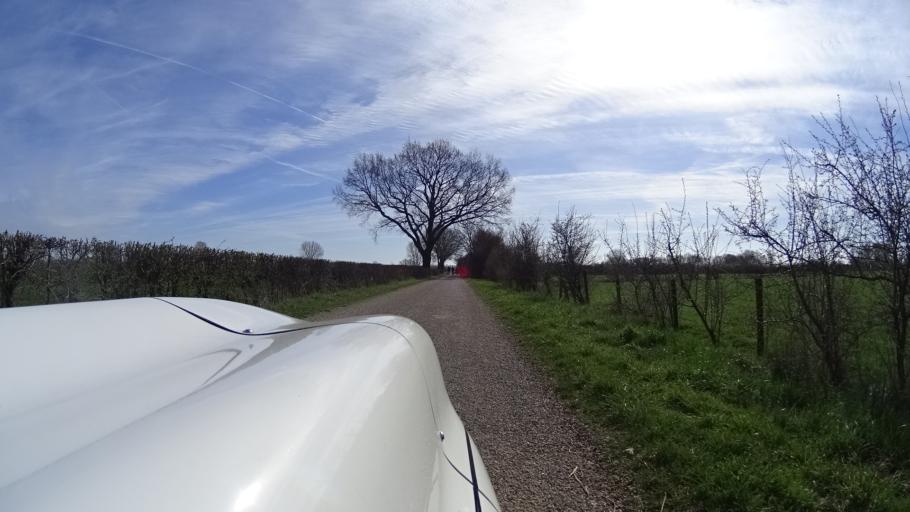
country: NL
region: Limburg
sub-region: Gemeente Gennep
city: Gennep
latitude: 51.7034
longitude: 5.9494
